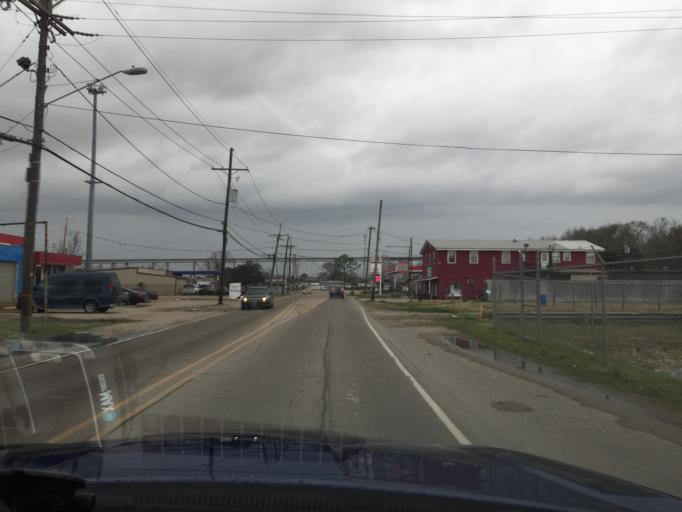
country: US
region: Louisiana
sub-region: Jefferson Parish
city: Bridge City
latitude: 29.9293
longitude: -90.1591
